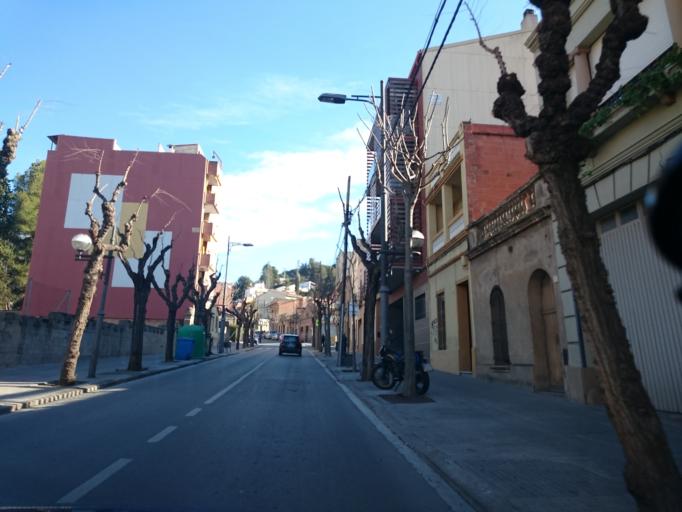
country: ES
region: Catalonia
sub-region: Provincia de Barcelona
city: Molins de Rei
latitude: 41.4156
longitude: 2.0206
